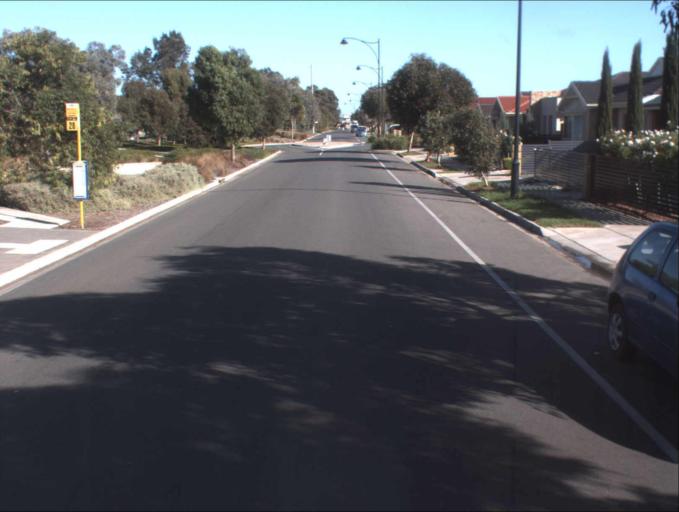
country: AU
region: South Australia
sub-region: Charles Sturt
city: Woodville North
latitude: -34.8560
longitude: 138.5533
